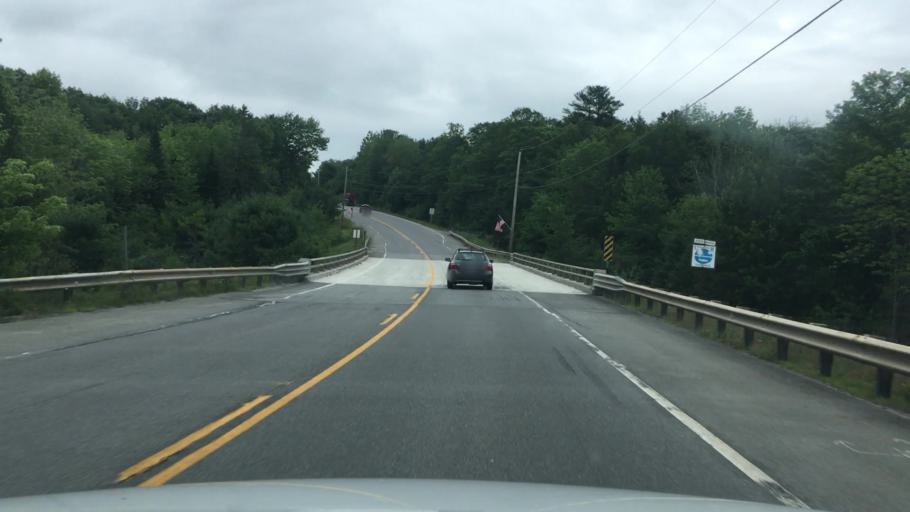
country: US
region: Maine
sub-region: Penobscot County
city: Bradley
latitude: 44.8271
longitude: -68.3761
